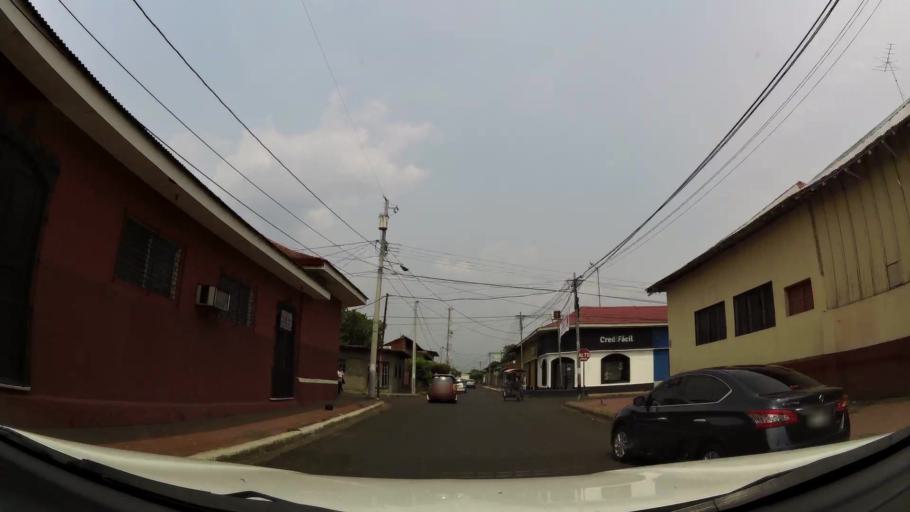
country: NI
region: Chinandega
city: Chinandega
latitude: 12.6268
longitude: -87.1317
